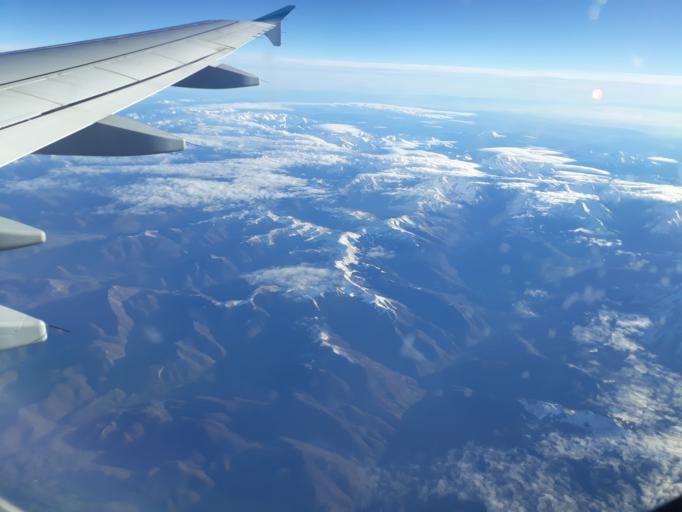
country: FR
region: Midi-Pyrenees
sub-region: Departement des Hautes-Pyrenees
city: Capvern
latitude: 43.1087
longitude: 0.3320
